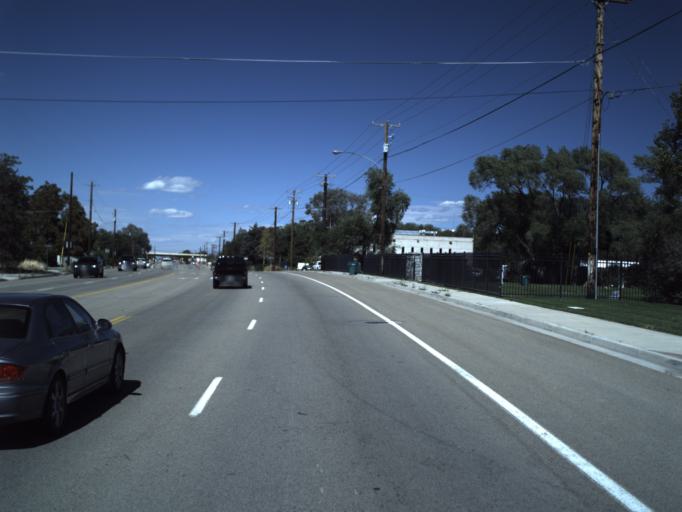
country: US
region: Utah
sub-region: Salt Lake County
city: Bluffdale
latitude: 40.4923
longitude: -111.9388
